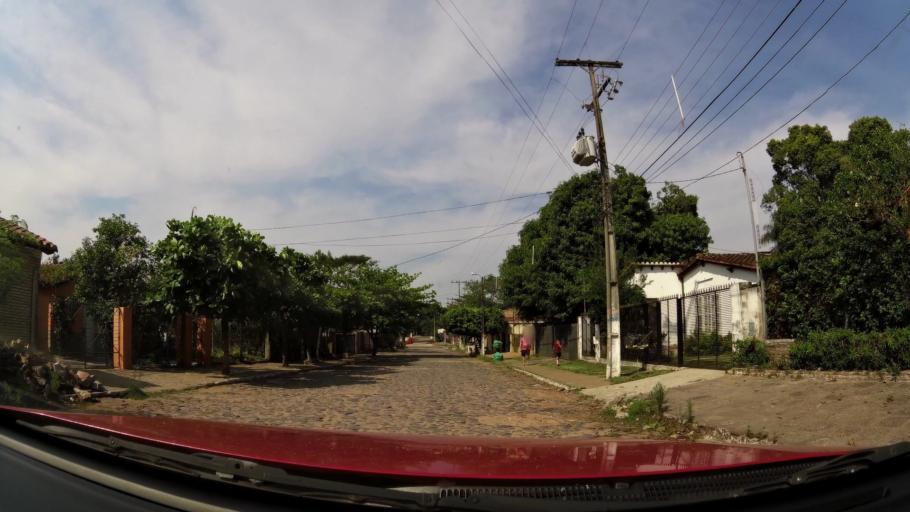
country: PY
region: Central
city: Fernando de la Mora
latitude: -25.2623
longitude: -57.5523
